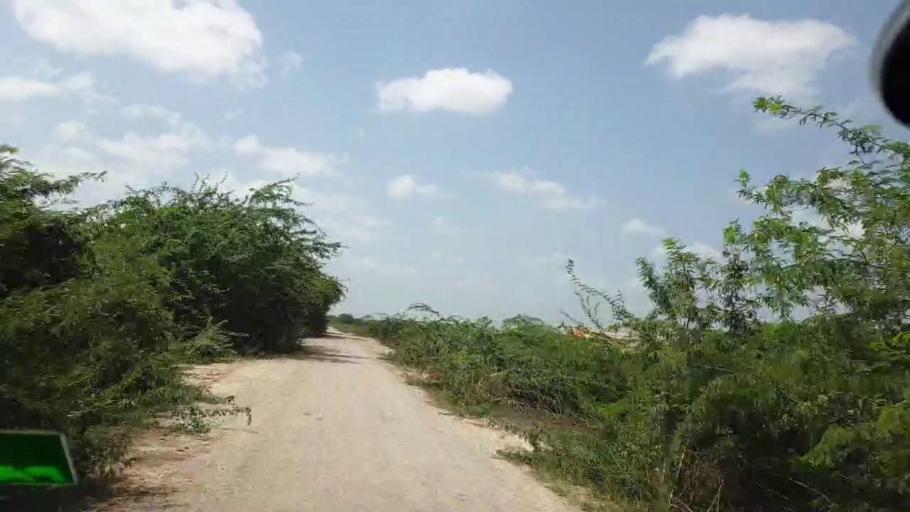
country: PK
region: Sindh
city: Kadhan
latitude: 24.5517
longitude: 69.1977
